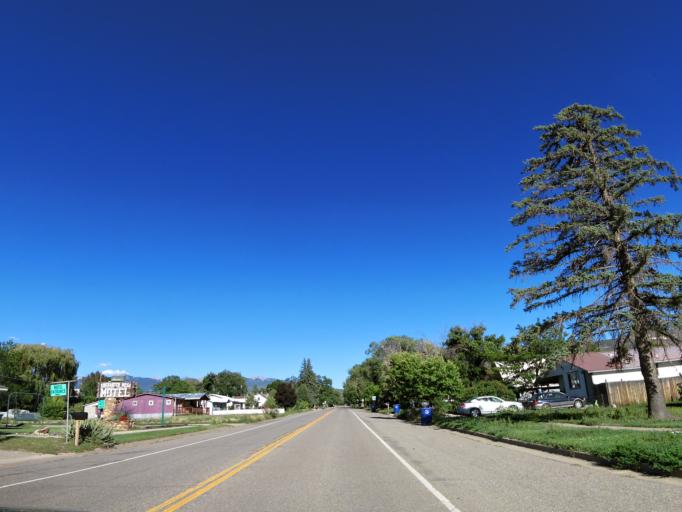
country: US
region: Colorado
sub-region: Montezuma County
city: Mancos
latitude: 37.3449
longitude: -108.3019
